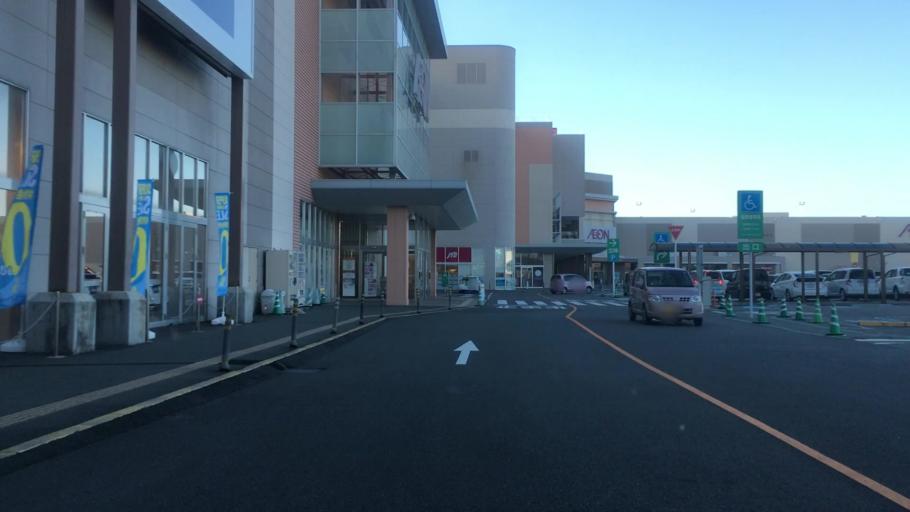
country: JP
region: Tottori
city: Tottori
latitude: 35.5228
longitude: 134.2015
